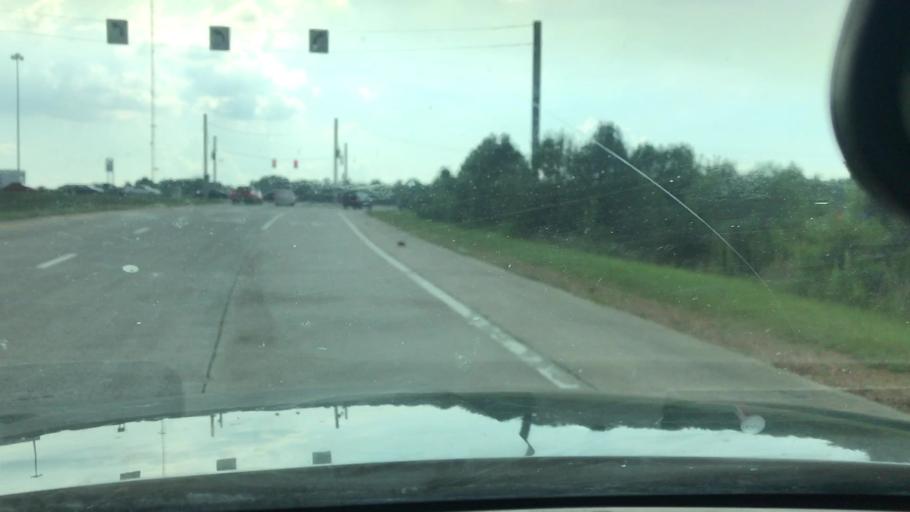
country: US
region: Tennessee
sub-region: Shelby County
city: Bartlett
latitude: 35.1766
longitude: -89.8352
